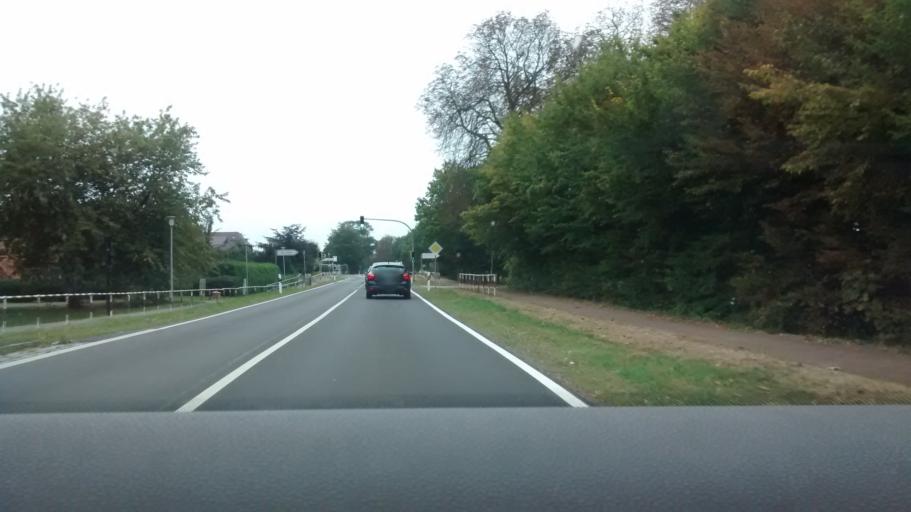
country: DE
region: Mecklenburg-Vorpommern
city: Mecklenburg
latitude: 53.8164
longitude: 11.4465
